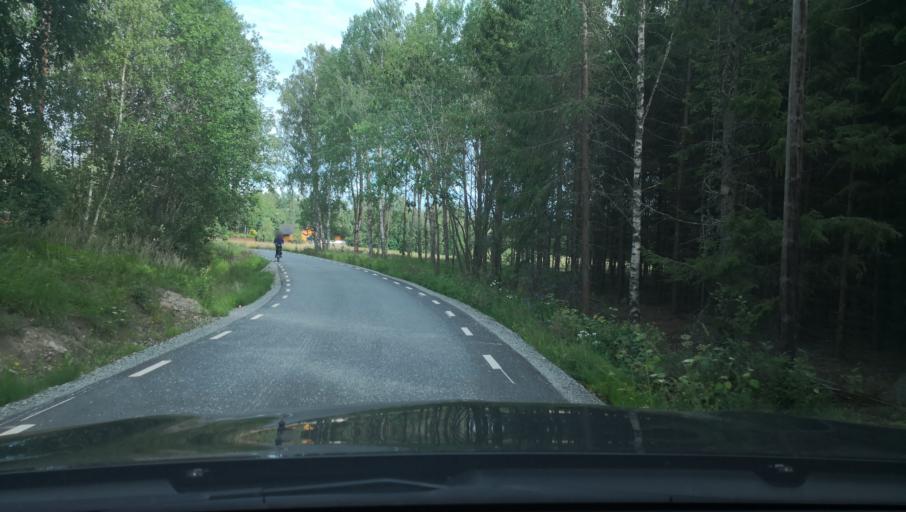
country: SE
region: Vaestmanland
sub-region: Surahammars Kommun
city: Surahammar
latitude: 59.6632
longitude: 16.1675
